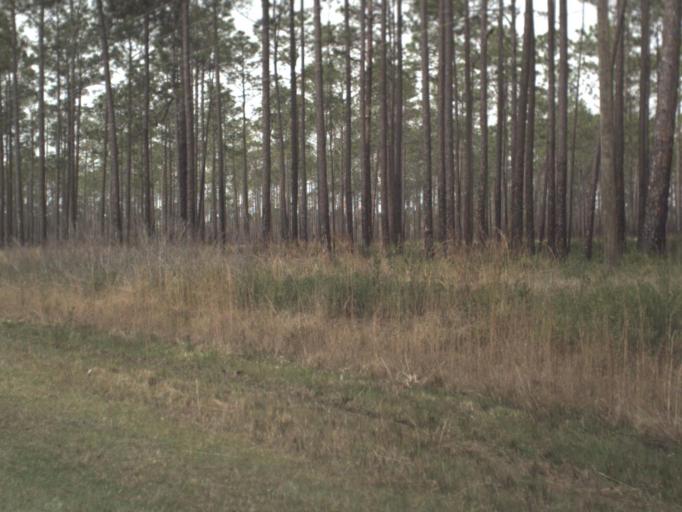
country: US
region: Florida
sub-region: Gulf County
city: Wewahitchka
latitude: 30.1500
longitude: -84.9703
